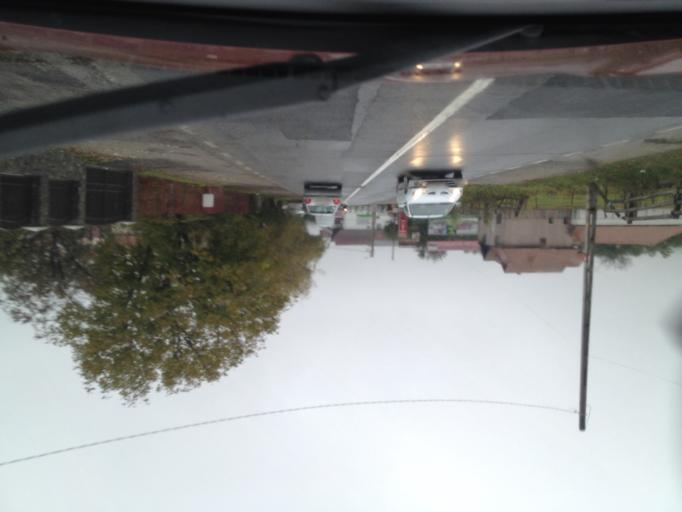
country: RO
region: Brasov
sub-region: Comuna Zarnesti
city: Tohanu Nou
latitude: 45.5317
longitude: 25.3737
